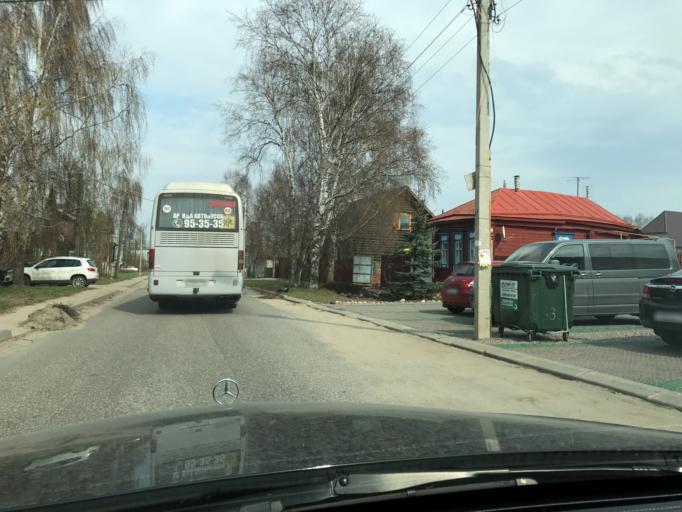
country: RU
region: Vladimir
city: Suzdal'
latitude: 56.4121
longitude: 40.4325
